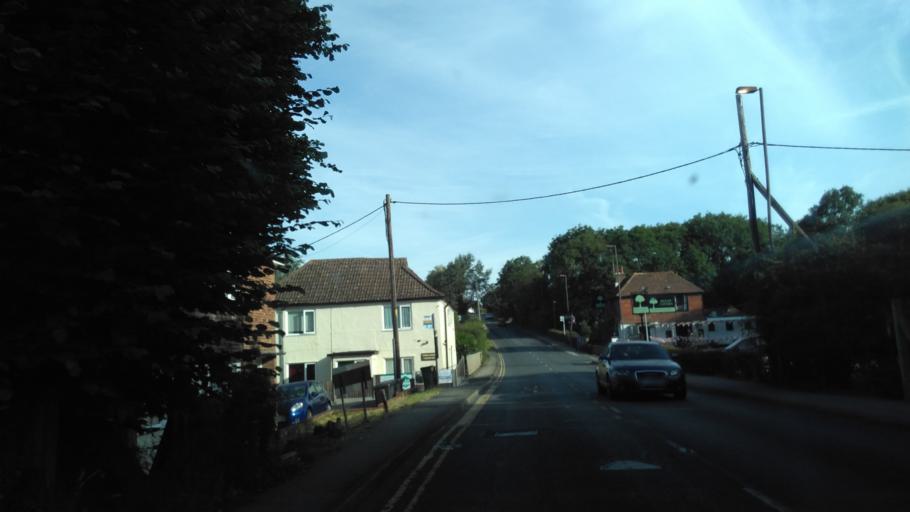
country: GB
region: England
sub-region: Kent
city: Blean
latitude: 51.3014
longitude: 1.0476
